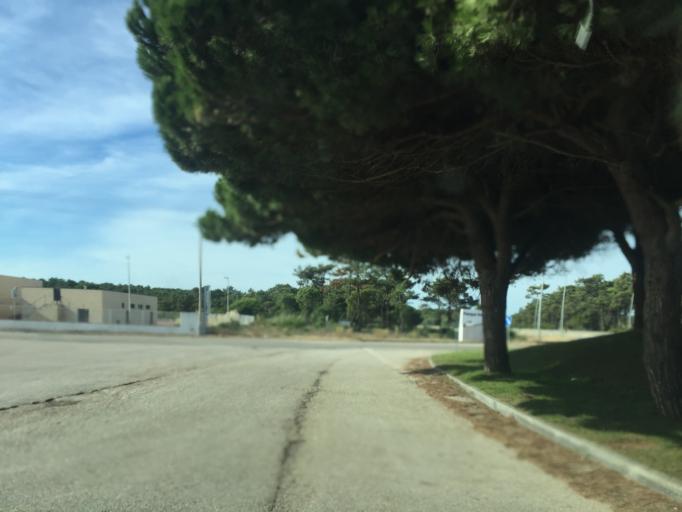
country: PT
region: Coimbra
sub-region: Figueira da Foz
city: Figueira da Foz
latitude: 40.1219
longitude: -8.8524
